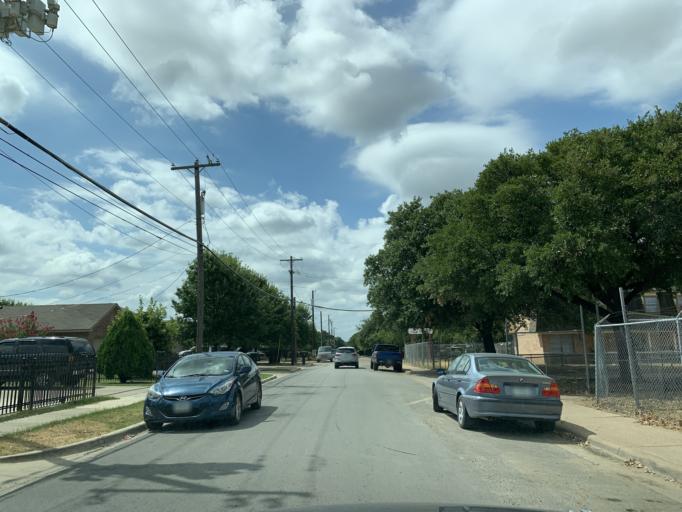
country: US
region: Texas
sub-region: Dallas County
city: Cockrell Hill
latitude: 32.7625
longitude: -96.8688
